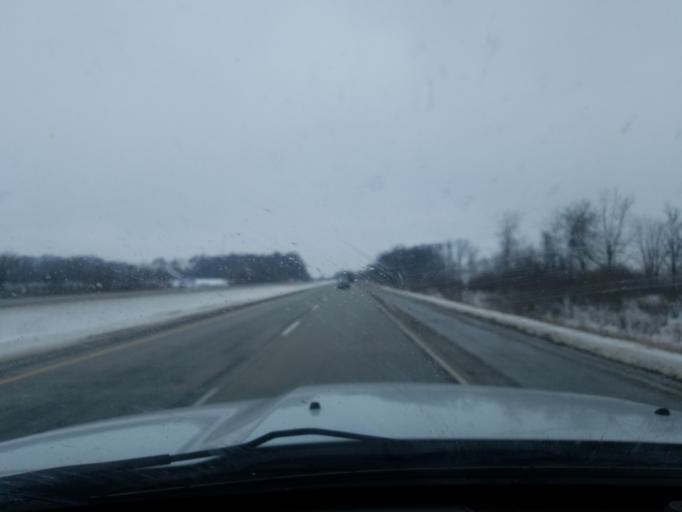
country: US
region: Indiana
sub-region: Marshall County
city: Argos
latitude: 41.1595
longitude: -86.2396
